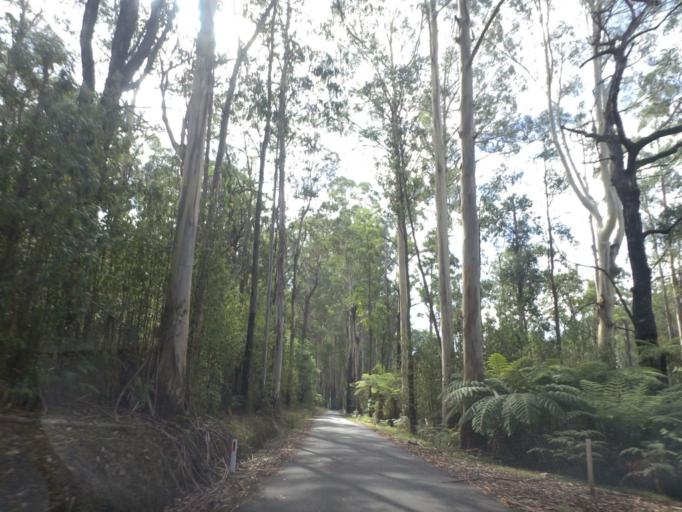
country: AU
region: Victoria
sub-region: Yarra Ranges
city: Millgrove
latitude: -37.5903
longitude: 145.6976
